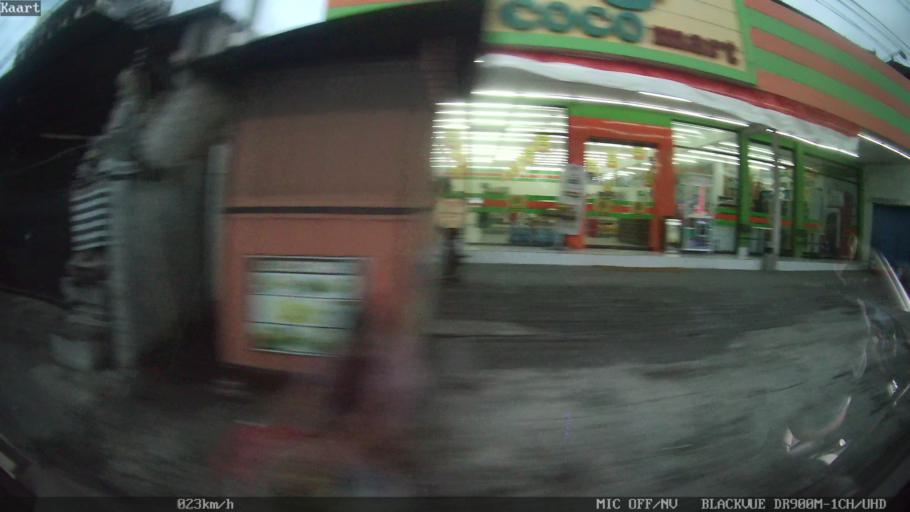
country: ID
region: Bali
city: Banjar Kertajiwa
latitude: -8.6272
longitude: 115.2648
